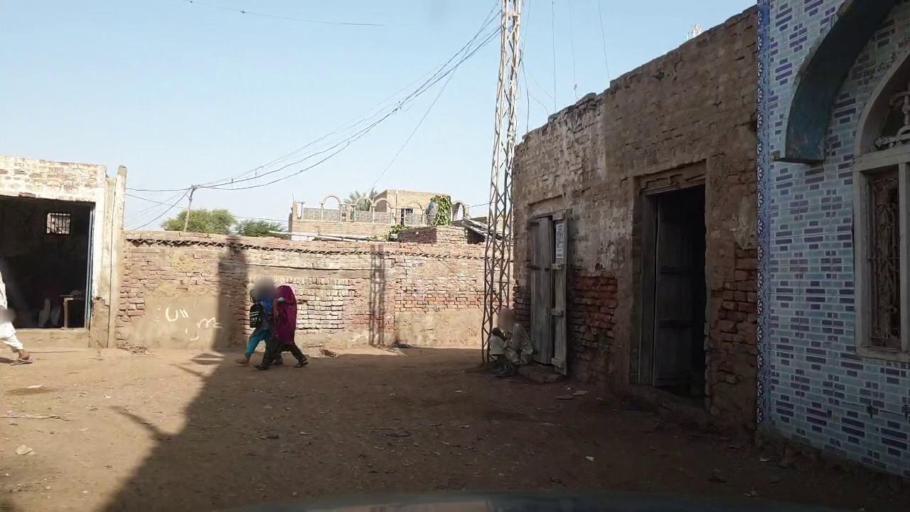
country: PK
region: Sindh
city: Tando Muhammad Khan
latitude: 25.1603
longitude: 68.3872
